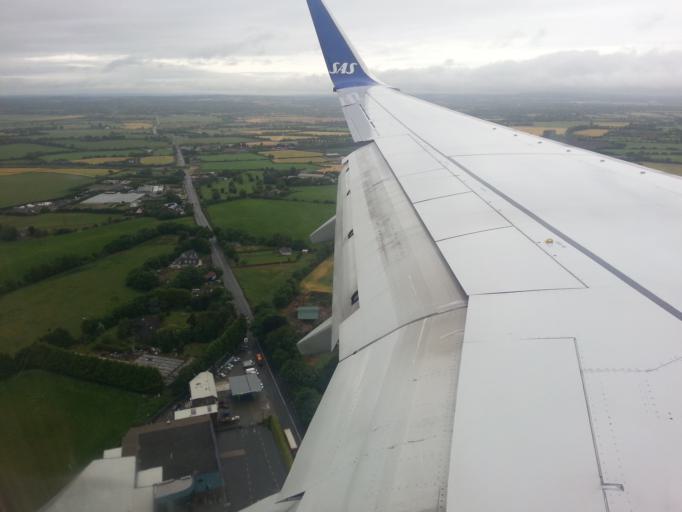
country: IE
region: Leinster
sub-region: Dublin City
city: Finglas
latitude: 53.4254
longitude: -6.3279
